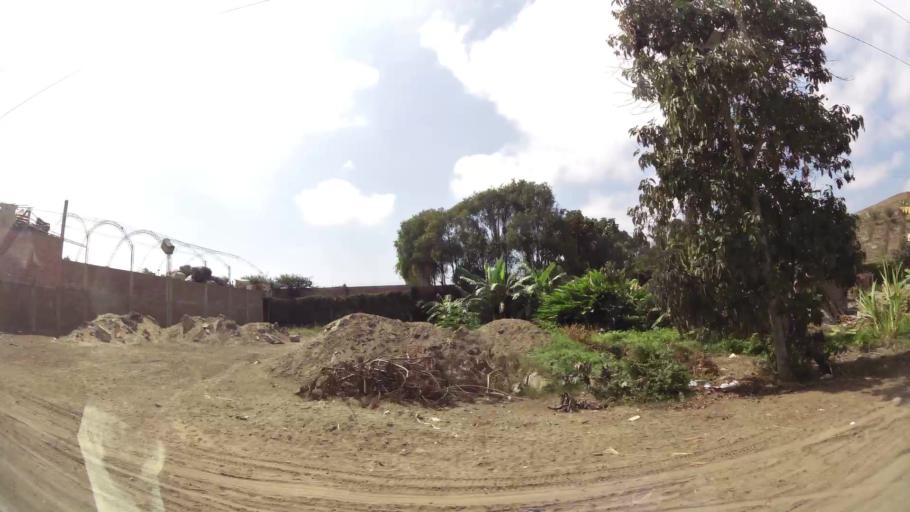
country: PE
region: Lima
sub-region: Provincia de Canete
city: Mala
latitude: -12.6765
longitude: -76.6290
